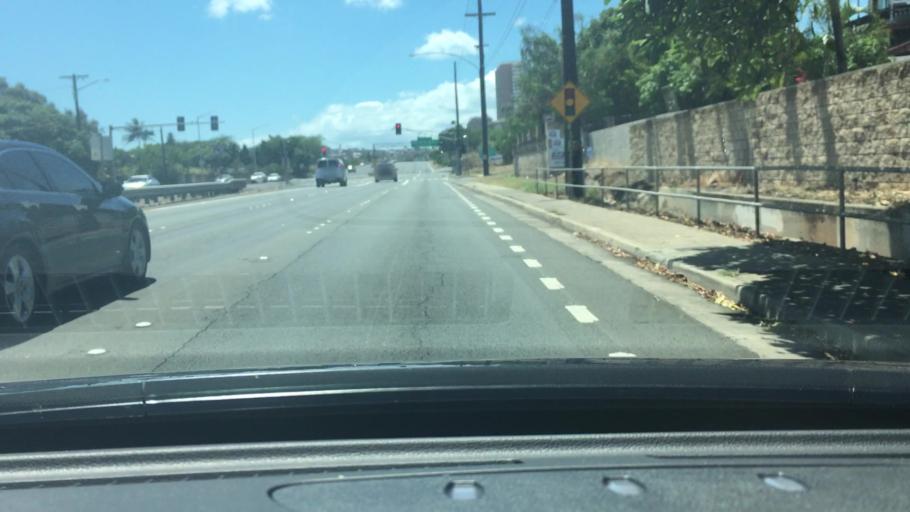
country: US
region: Hawaii
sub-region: Honolulu County
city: Honolulu
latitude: 21.2779
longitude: -157.7788
